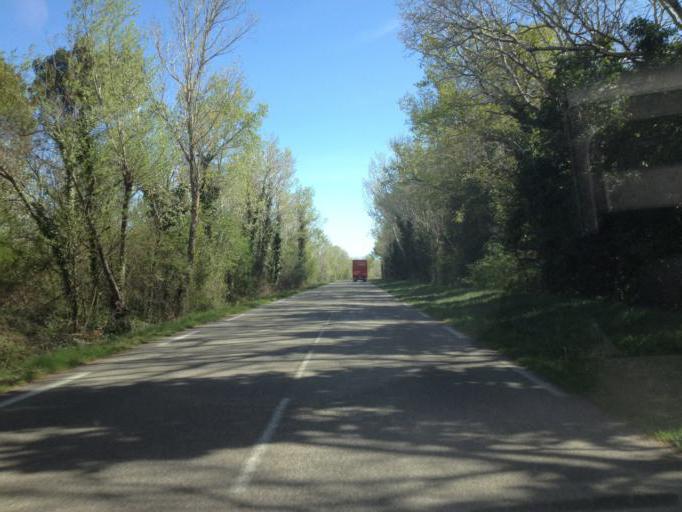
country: FR
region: Provence-Alpes-Cote d'Azur
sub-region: Departement du Vaucluse
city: Caderousse
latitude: 44.1292
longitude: 4.7243
